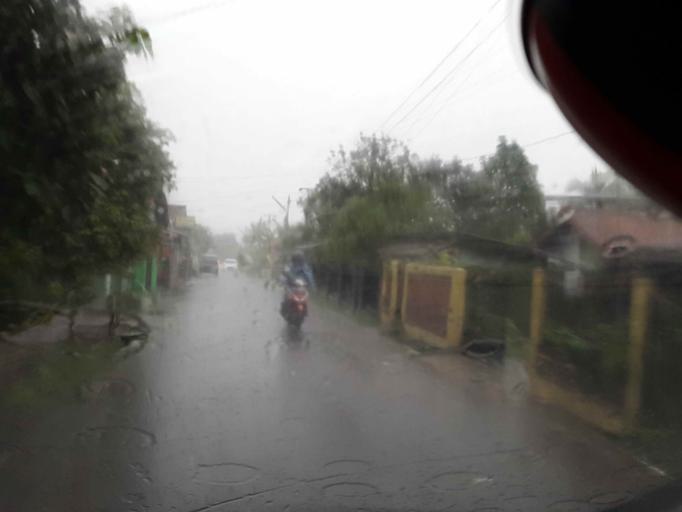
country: ID
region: West Java
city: Cimahi
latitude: -6.9000
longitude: 107.5017
